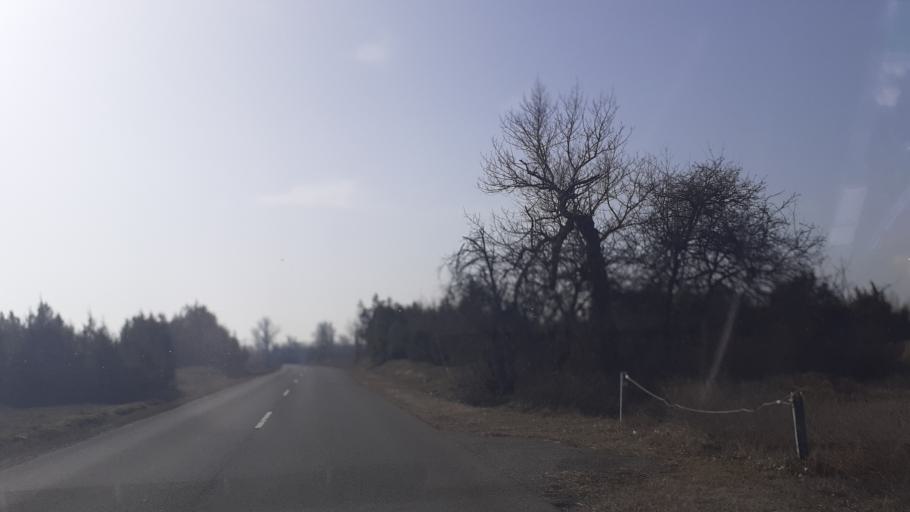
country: HU
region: Pest
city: Orkeny
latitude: 47.1049
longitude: 19.3960
